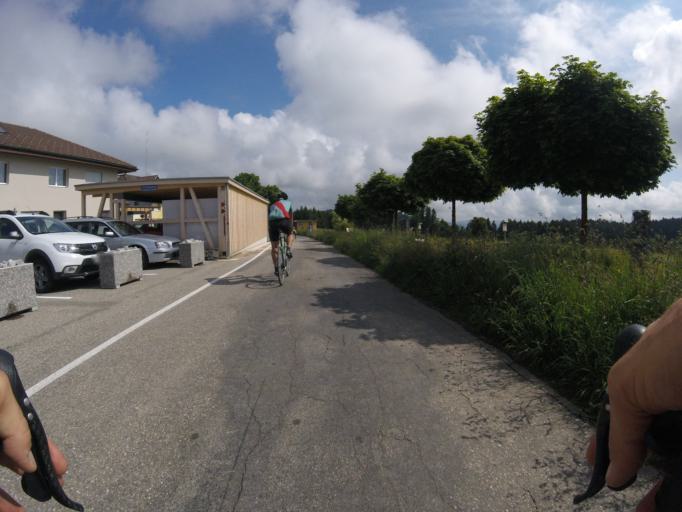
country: CH
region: Bern
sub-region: Bern-Mittelland District
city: Walkringen
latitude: 46.9560
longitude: 7.6028
